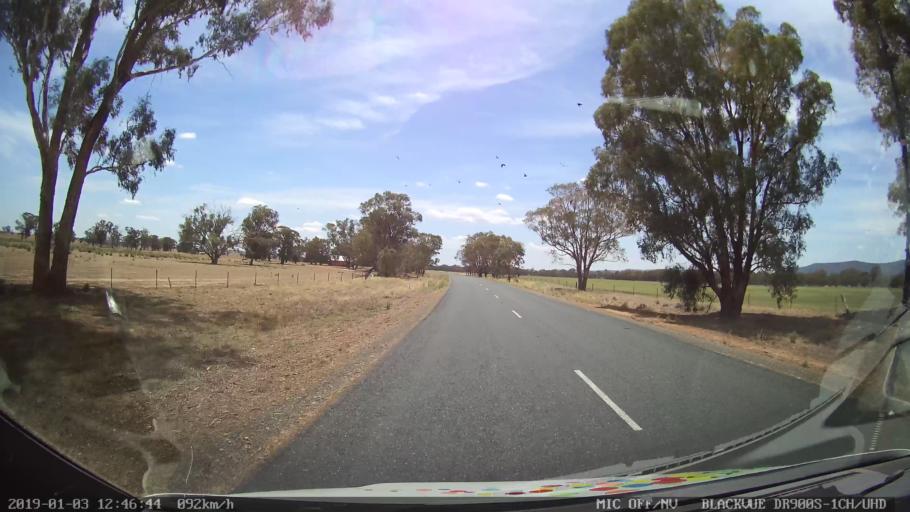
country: AU
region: New South Wales
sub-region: Weddin
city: Grenfell
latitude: -33.7357
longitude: 148.2373
